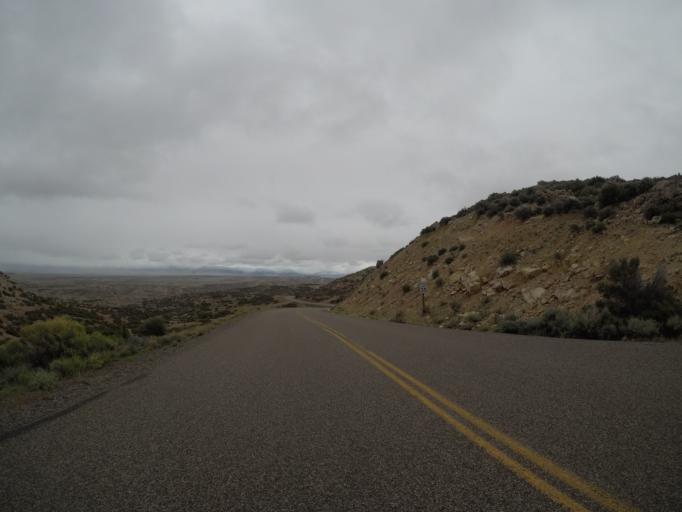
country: US
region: Wyoming
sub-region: Big Horn County
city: Lovell
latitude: 45.0260
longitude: -108.2642
